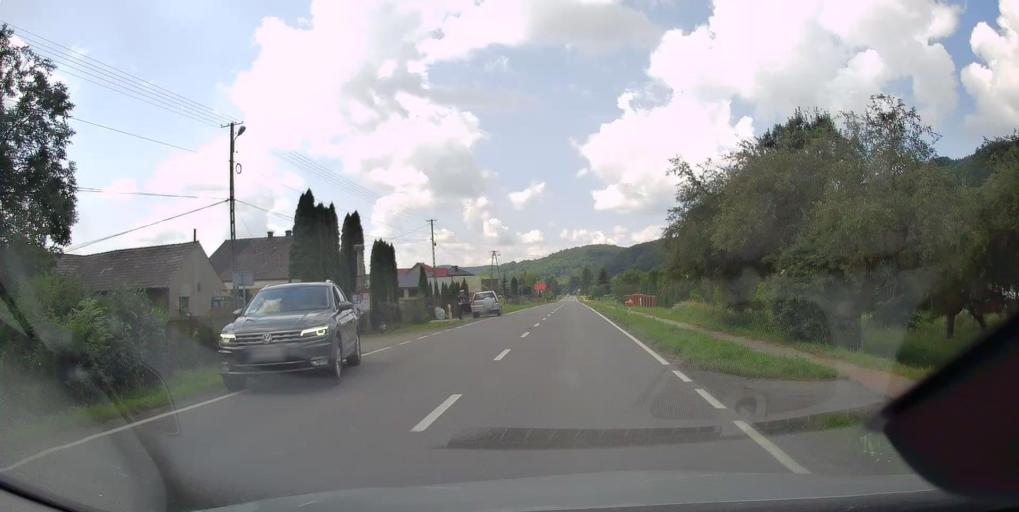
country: PL
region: Lesser Poland Voivodeship
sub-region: Powiat tarnowski
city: Wielka Wies
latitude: 49.9207
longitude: 20.8262
